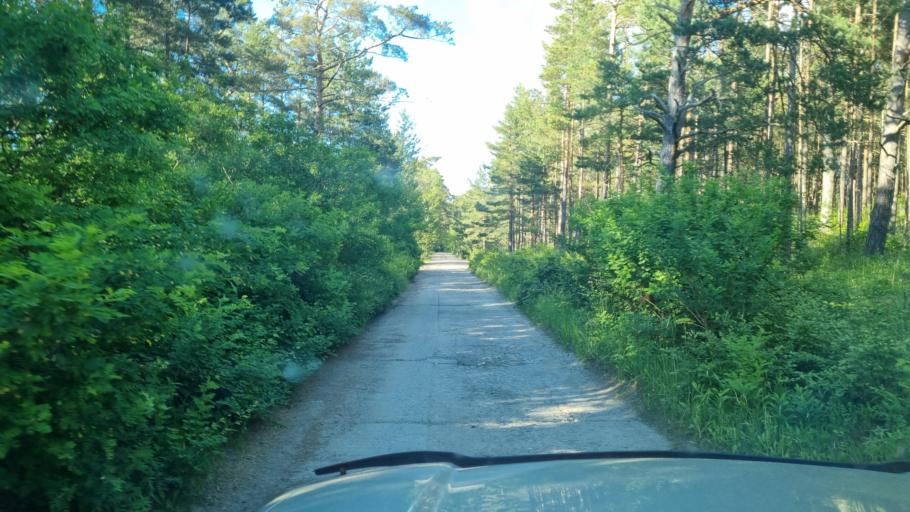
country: LV
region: Ventspils
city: Ventspils
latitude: 57.3656
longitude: 21.5143
